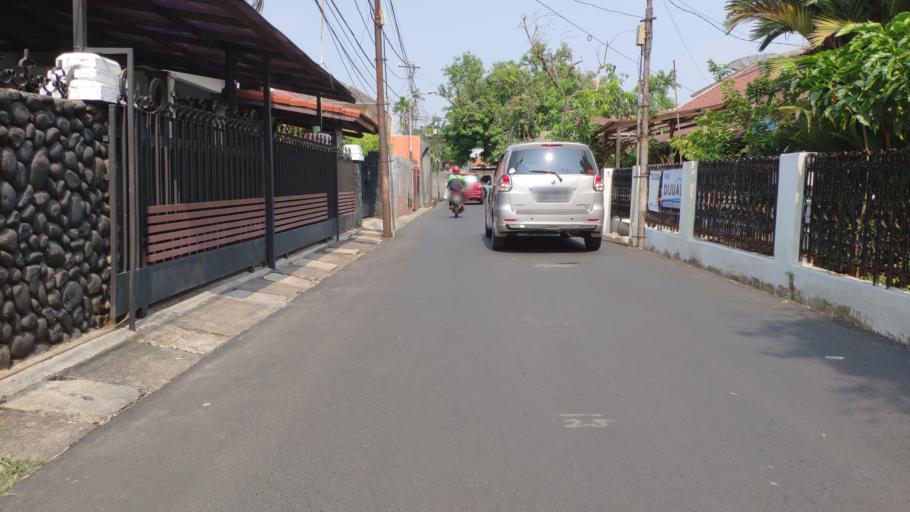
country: ID
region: Jakarta Raya
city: Jakarta
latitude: -6.2508
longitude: 106.8112
